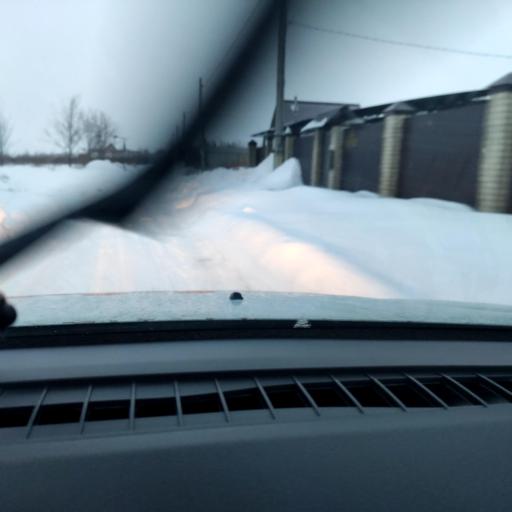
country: RU
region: Samara
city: Dubovyy Umet
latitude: 53.0302
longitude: 50.2299
